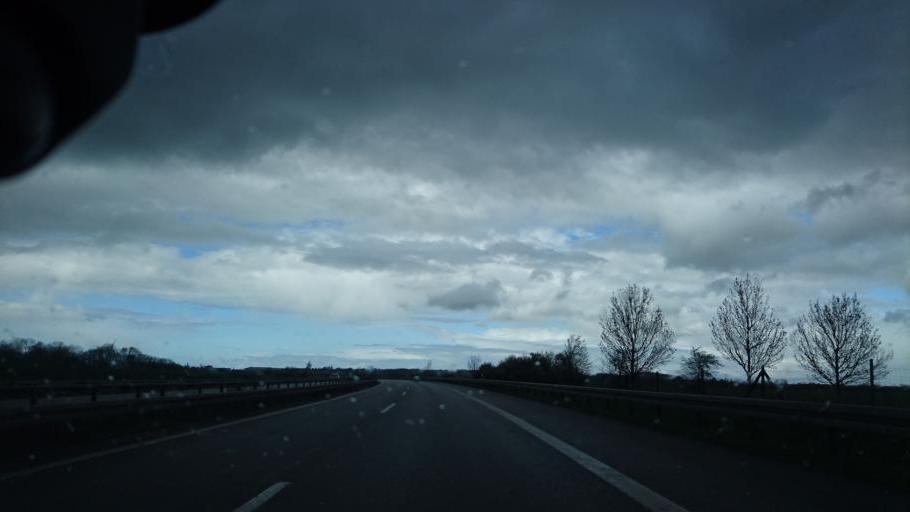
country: DE
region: Mecklenburg-Vorpommern
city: Kritzmow
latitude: 54.0327
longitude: 12.0582
